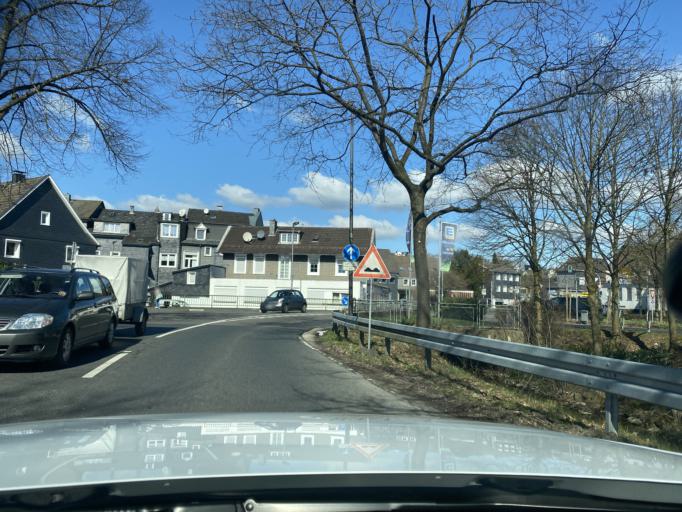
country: DE
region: North Rhine-Westphalia
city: Wipperfurth
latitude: 51.1175
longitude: 7.4000
